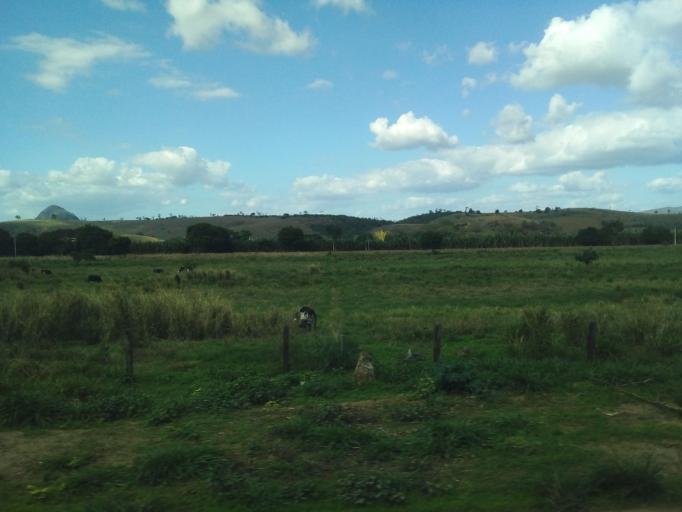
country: BR
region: Minas Gerais
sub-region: Conselheiro Pena
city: Conselheiro Pena
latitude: -18.9981
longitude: -41.5923
